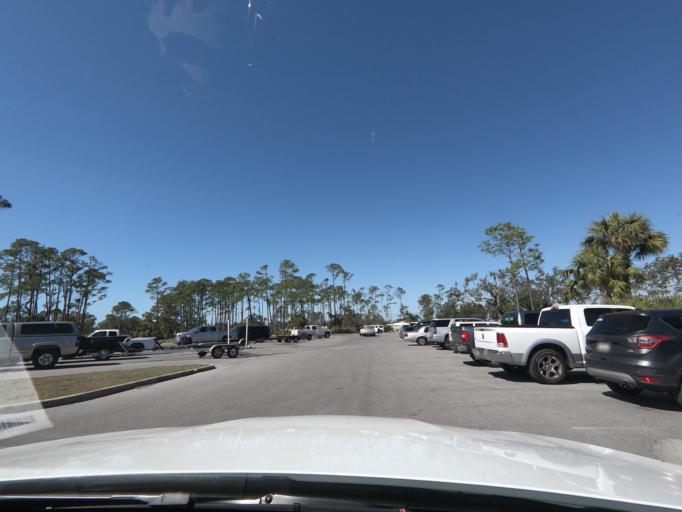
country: US
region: Florida
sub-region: Bay County
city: Lower Grand Lagoon
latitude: 30.1320
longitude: -85.7311
